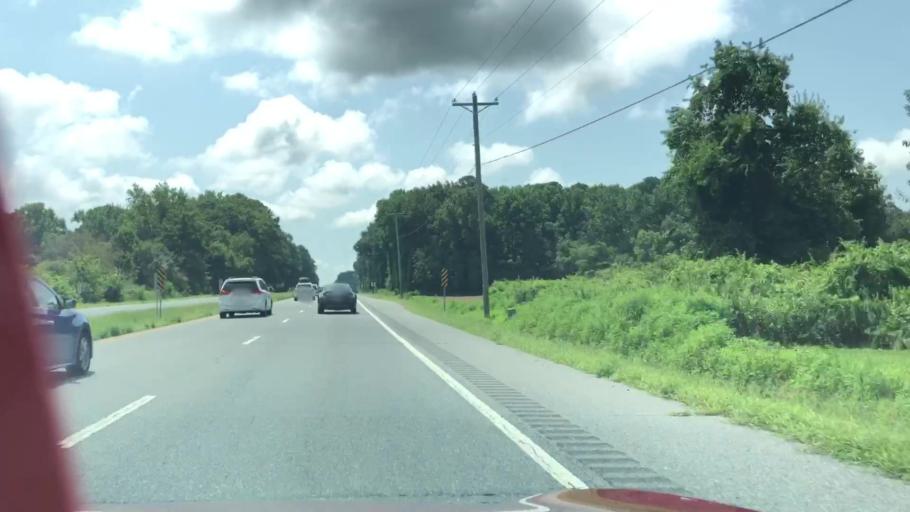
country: US
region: Virginia
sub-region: Northampton County
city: Cape Charles
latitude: 37.2627
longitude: -75.9742
